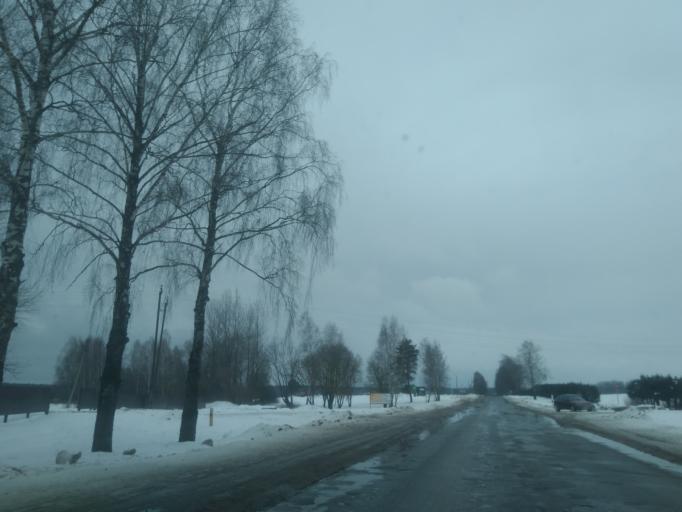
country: BY
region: Minsk
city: Ivyanyets
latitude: 53.9001
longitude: 26.7519
